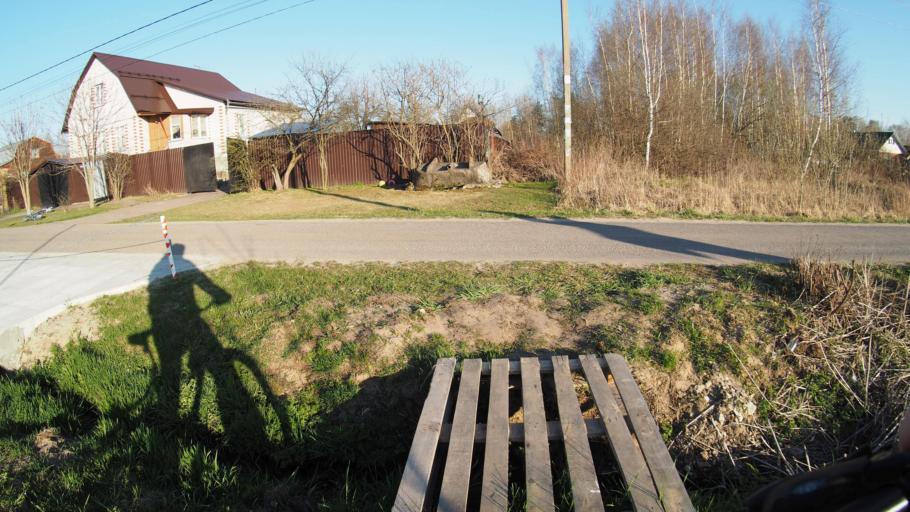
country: RU
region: Moskovskaya
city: Malyshevo
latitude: 55.4876
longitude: 38.3506
